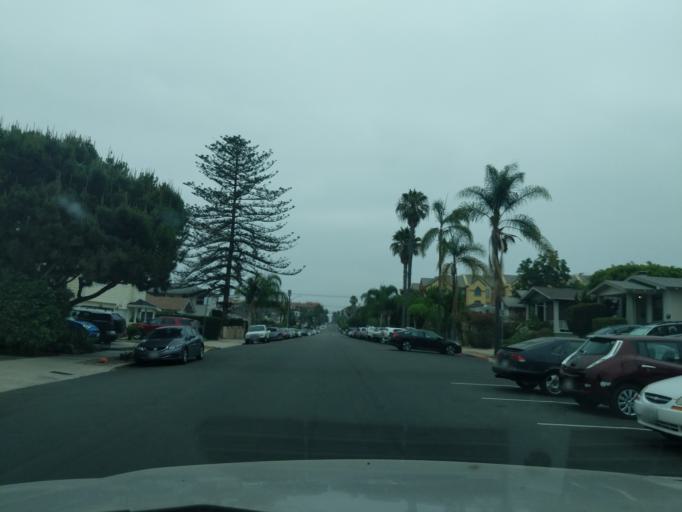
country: US
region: California
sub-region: San Diego County
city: San Diego
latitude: 32.7509
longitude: -117.1425
